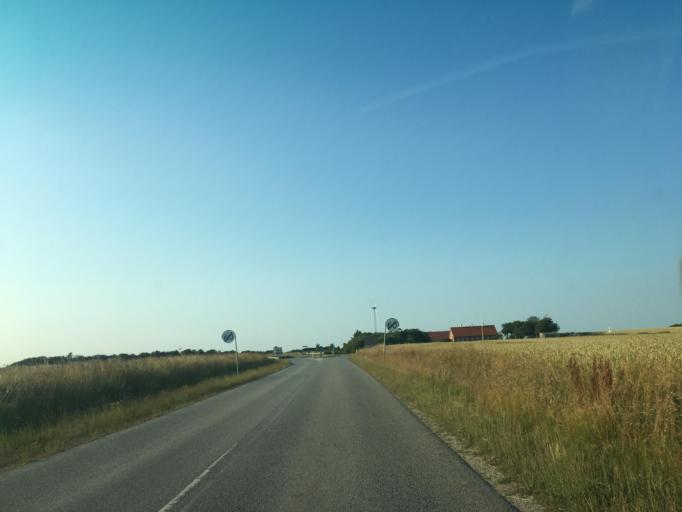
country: DK
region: North Denmark
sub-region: Thisted Kommune
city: Hurup
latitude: 56.7584
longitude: 8.4243
